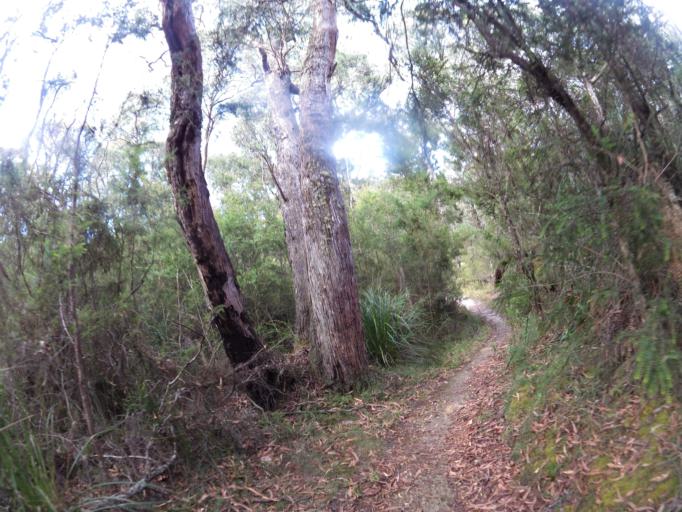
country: AU
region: Victoria
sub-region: Colac-Otway
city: Colac
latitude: -38.4910
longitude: 143.7037
